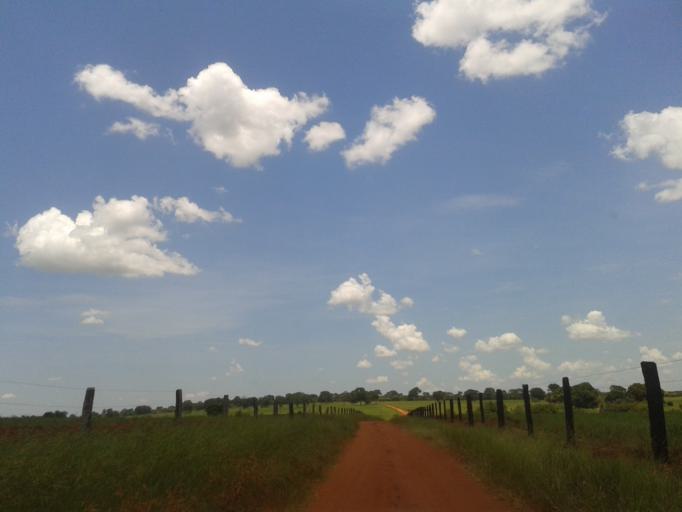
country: BR
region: Minas Gerais
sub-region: Santa Vitoria
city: Santa Vitoria
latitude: -19.2118
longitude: -50.4065
